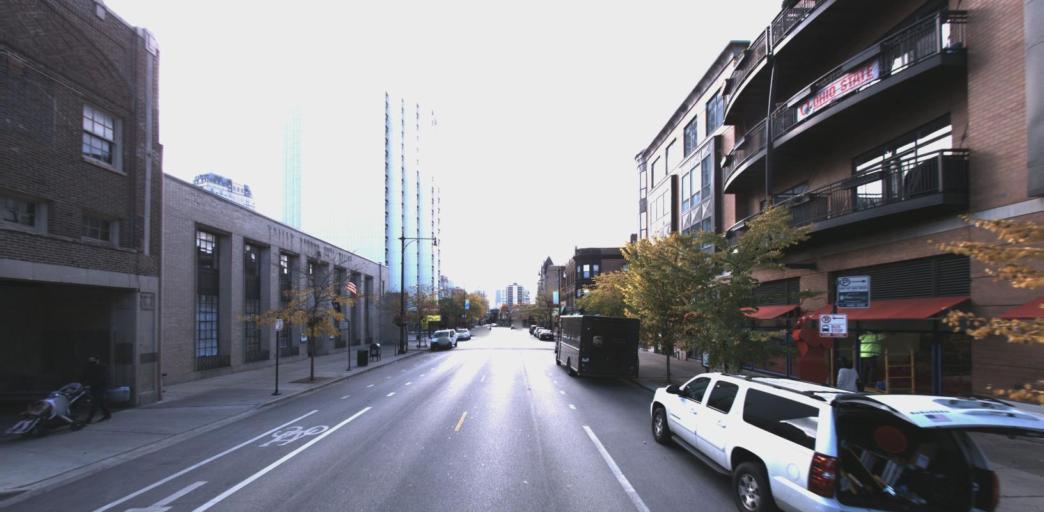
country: US
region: Illinois
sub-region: Cook County
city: Chicago
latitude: 41.9311
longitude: -87.6441
